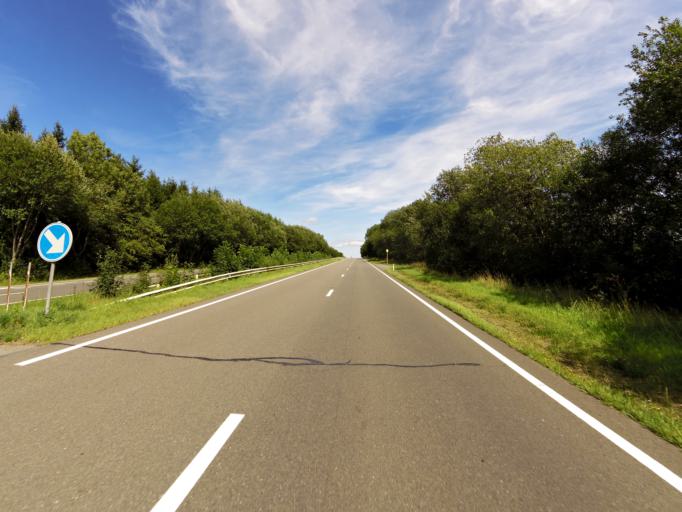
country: BE
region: Wallonia
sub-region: Province du Luxembourg
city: Tenneville
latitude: 50.0906
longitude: 5.4510
